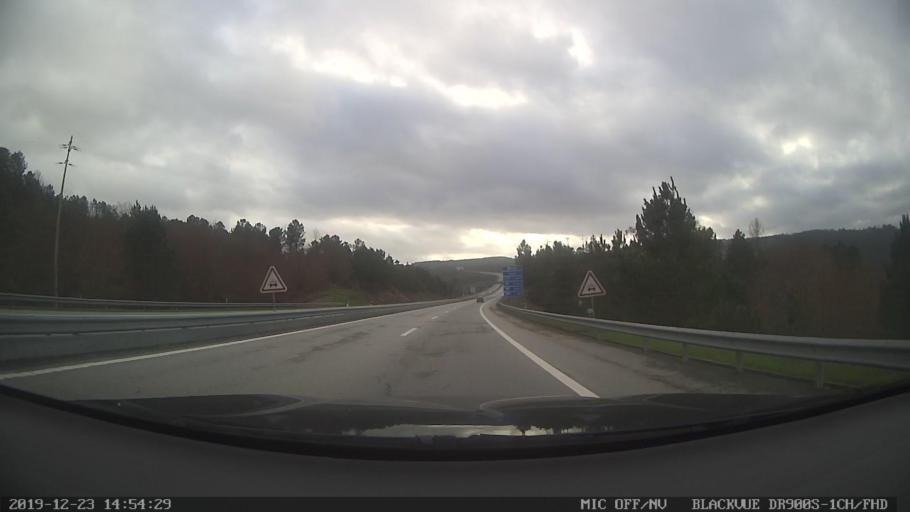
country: PT
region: Viseu
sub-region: Viseu
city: Campo
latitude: 40.7566
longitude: -7.9213
